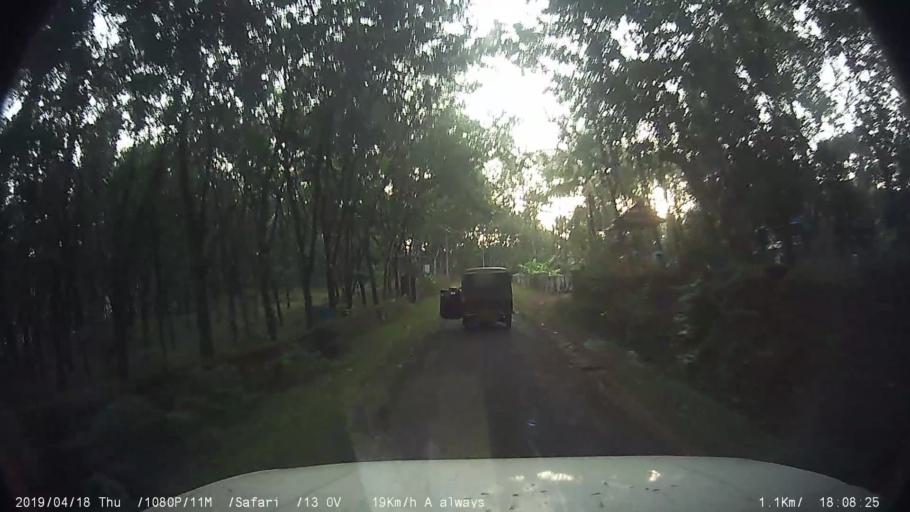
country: IN
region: Kerala
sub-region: Kottayam
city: Palackattumala
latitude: 9.7777
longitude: 76.5837
